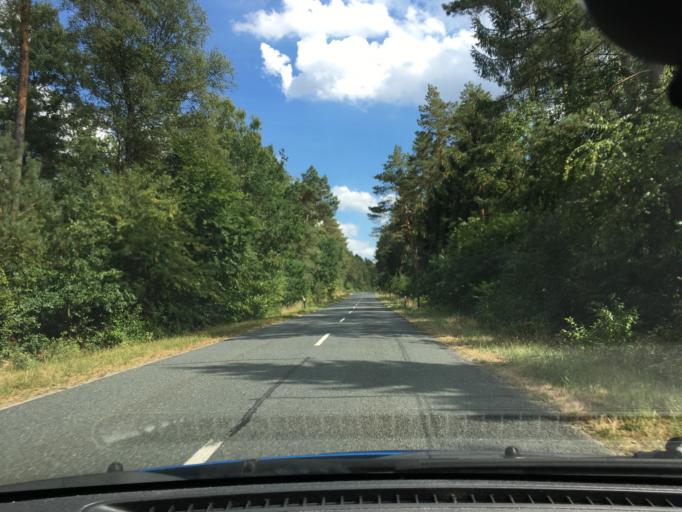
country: DE
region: Lower Saxony
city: Rehlingen
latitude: 53.0832
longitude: 10.2157
